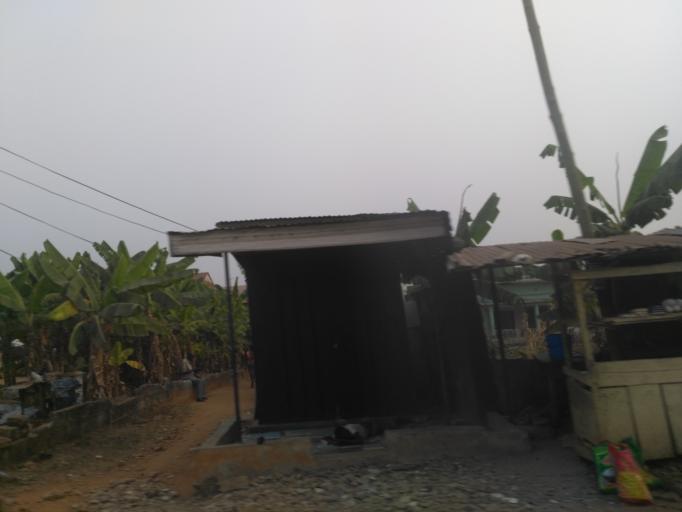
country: GH
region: Ashanti
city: Tafo
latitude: 6.7103
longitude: -1.6065
